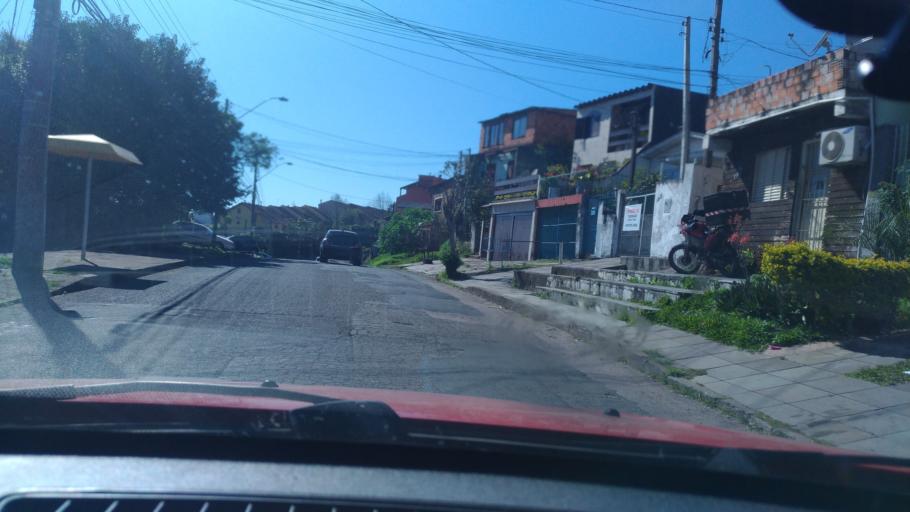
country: BR
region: Rio Grande do Sul
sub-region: Porto Alegre
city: Porto Alegre
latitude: -30.0346
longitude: -51.1493
